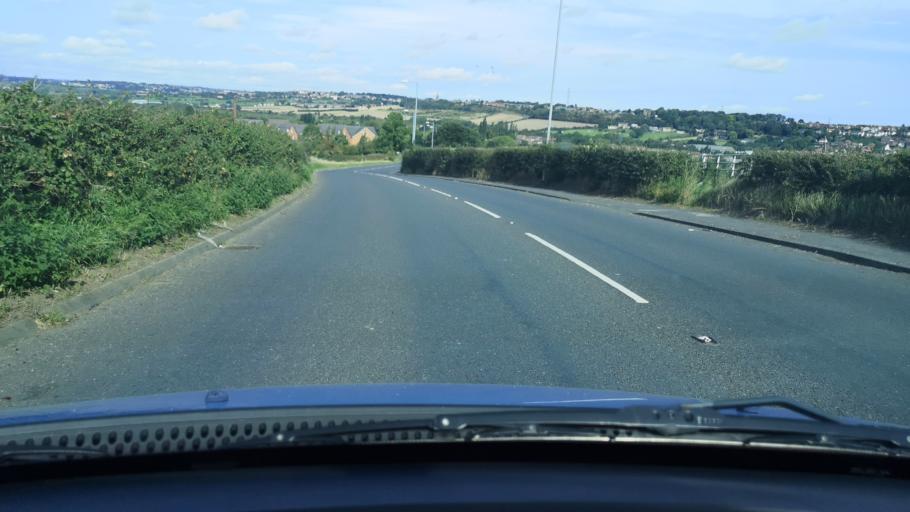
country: GB
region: England
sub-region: City and Borough of Wakefield
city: Horbury
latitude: 53.6516
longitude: -1.5743
